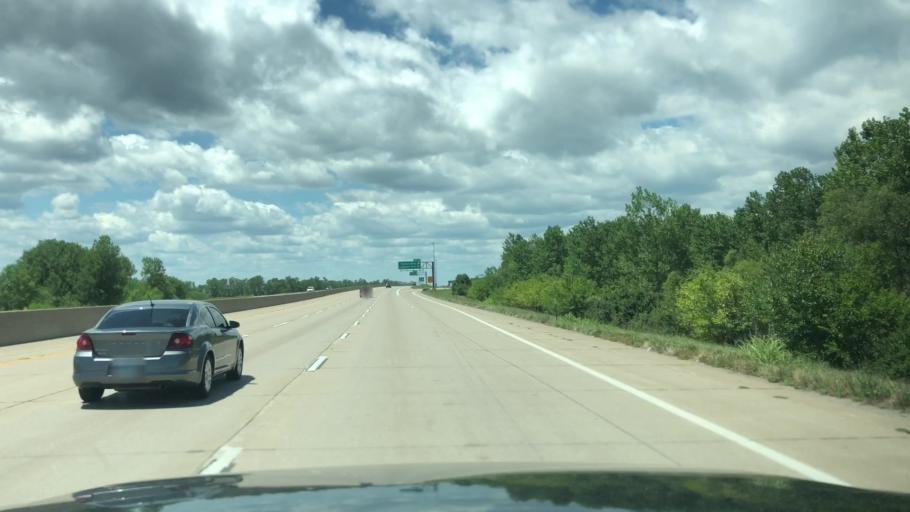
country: US
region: Missouri
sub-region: Saint Charles County
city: Saint Peters
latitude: 38.8191
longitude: -90.5556
